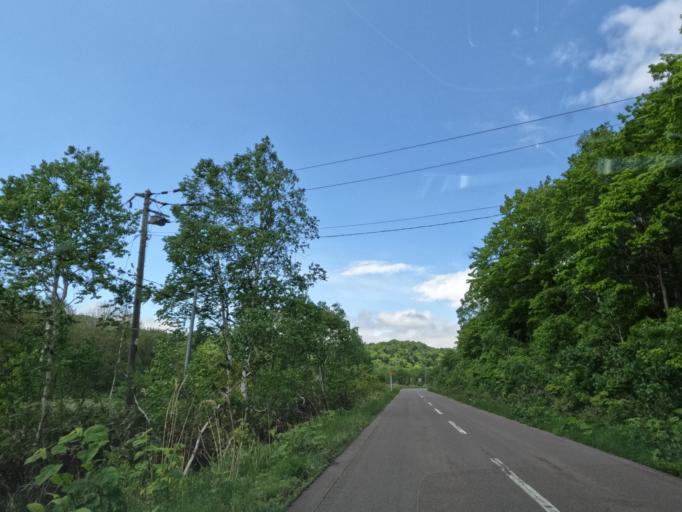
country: JP
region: Hokkaido
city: Tobetsu
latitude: 43.5164
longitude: 141.5885
